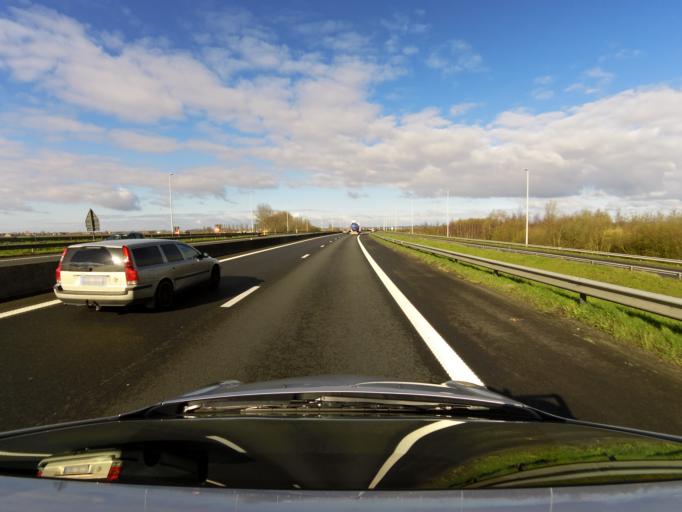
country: BE
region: Flanders
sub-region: Provincie West-Vlaanderen
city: Veurne
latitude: 51.0563
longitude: 2.6640
